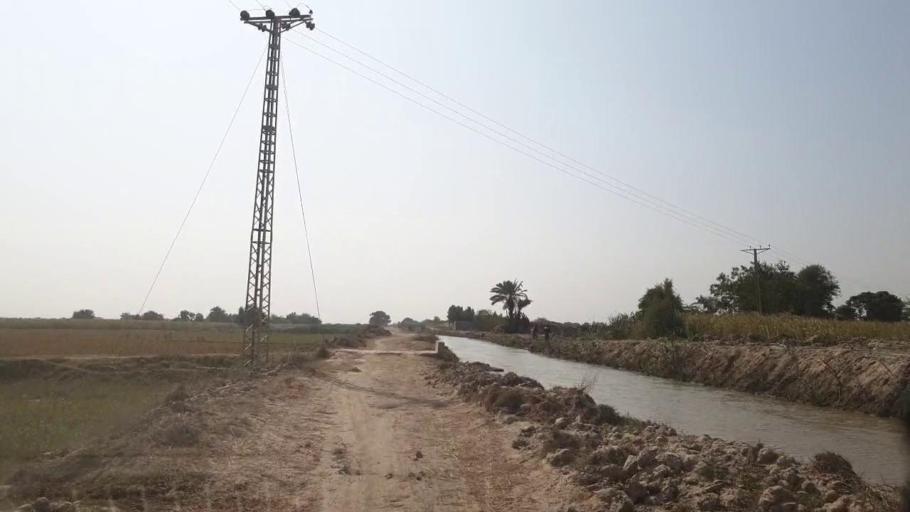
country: PK
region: Sindh
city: Bulri
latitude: 24.9608
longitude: 68.3894
